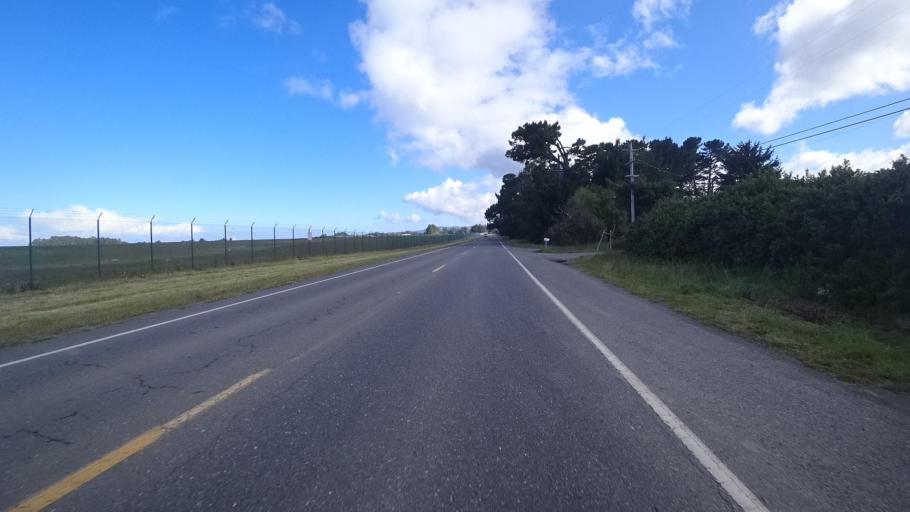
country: US
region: California
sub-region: Humboldt County
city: McKinleyville
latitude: 40.9708
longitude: -124.1006
